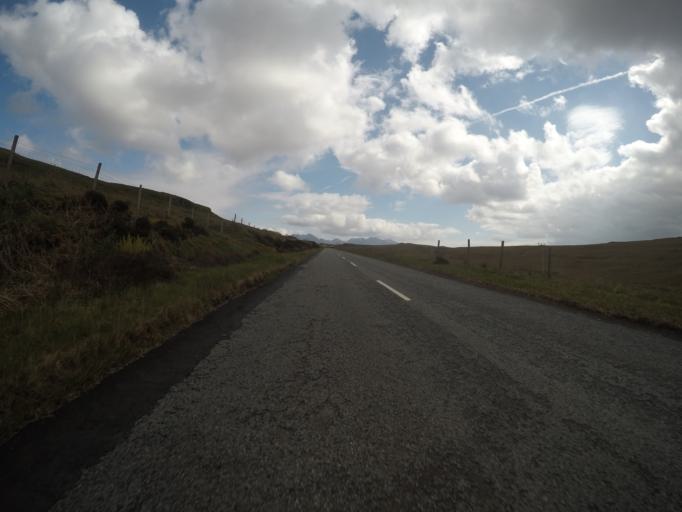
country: GB
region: Scotland
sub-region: Highland
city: Isle of Skye
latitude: 57.3235
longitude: -6.3305
